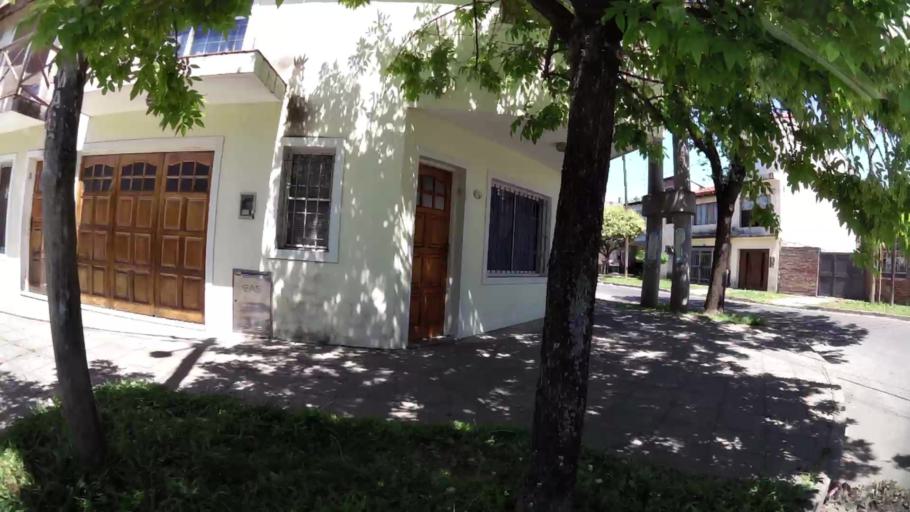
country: AR
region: Buenos Aires
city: Caseros
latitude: -34.5698
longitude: -58.5708
